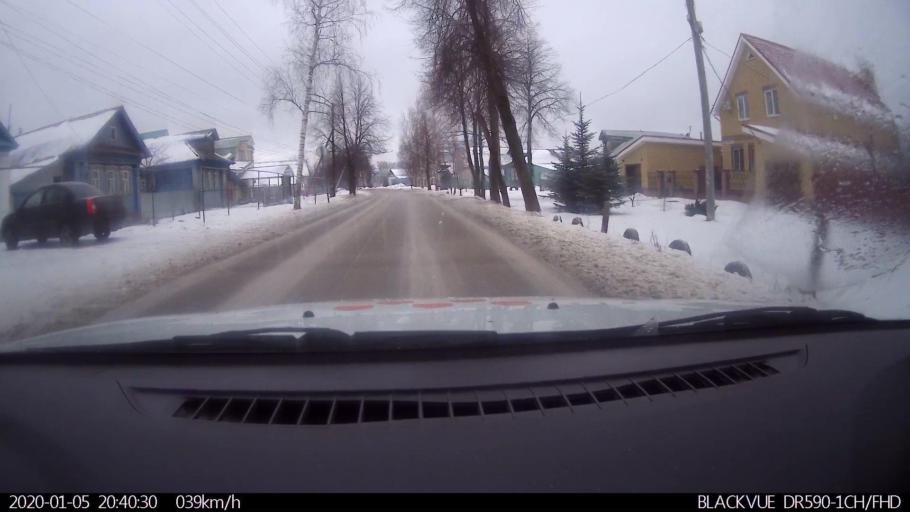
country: RU
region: Nizjnij Novgorod
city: Lukino
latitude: 56.4094
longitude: 43.7287
